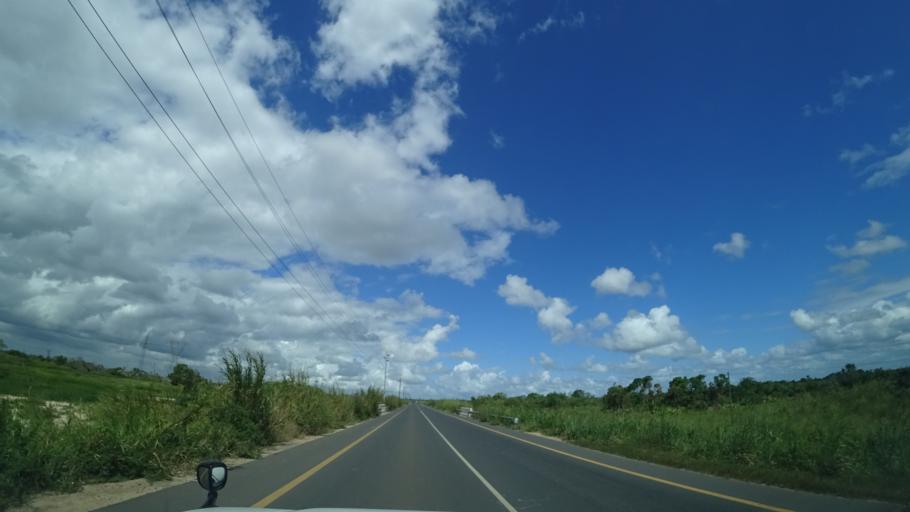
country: MZ
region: Sofala
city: Dondo
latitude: -19.5165
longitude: 34.6194
